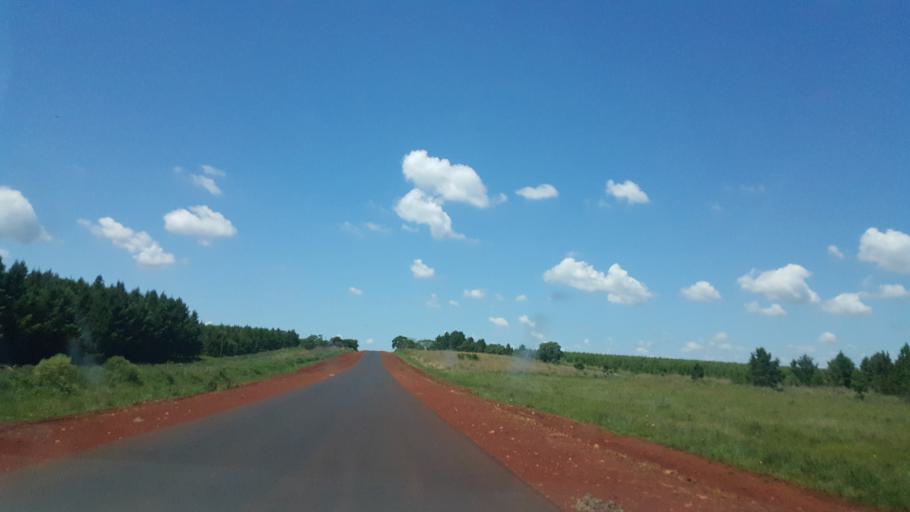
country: AR
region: Corrientes
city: Santo Tome
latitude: -28.4773
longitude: -56.0335
